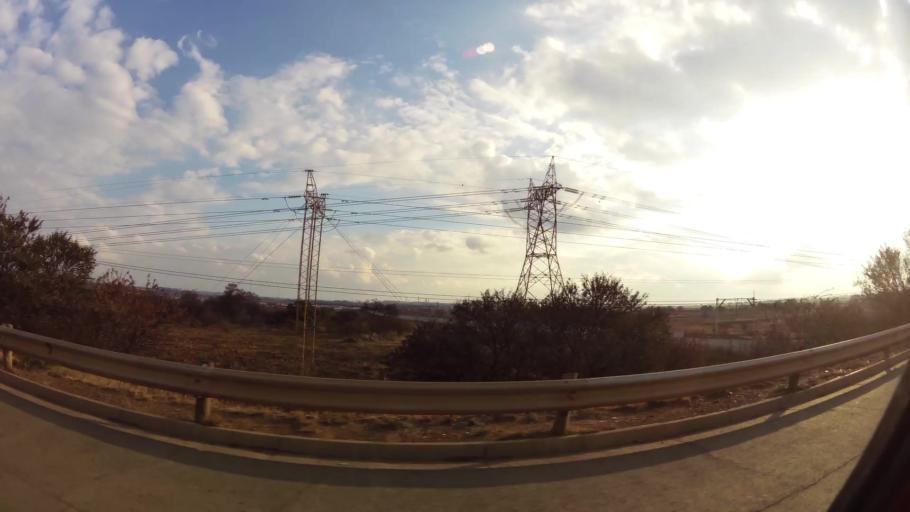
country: ZA
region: Gauteng
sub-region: Sedibeng District Municipality
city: Vereeniging
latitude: -26.6381
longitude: 27.8714
